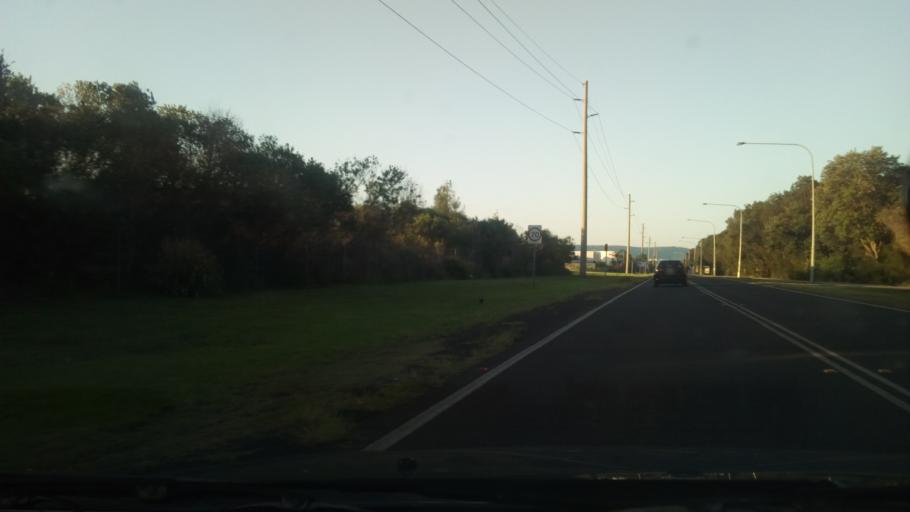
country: AU
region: New South Wales
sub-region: Wollongong
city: Fairy Meadow
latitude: -34.4049
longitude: 150.8997
